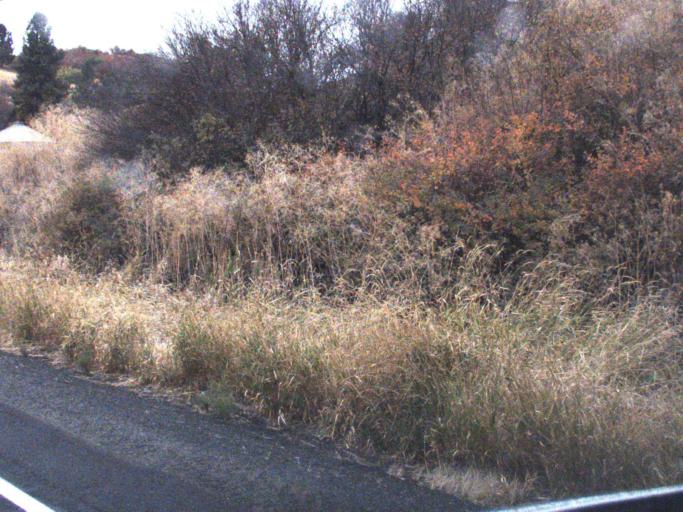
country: US
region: Washington
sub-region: Whitman County
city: Colfax
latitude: 46.8606
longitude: -117.3498
